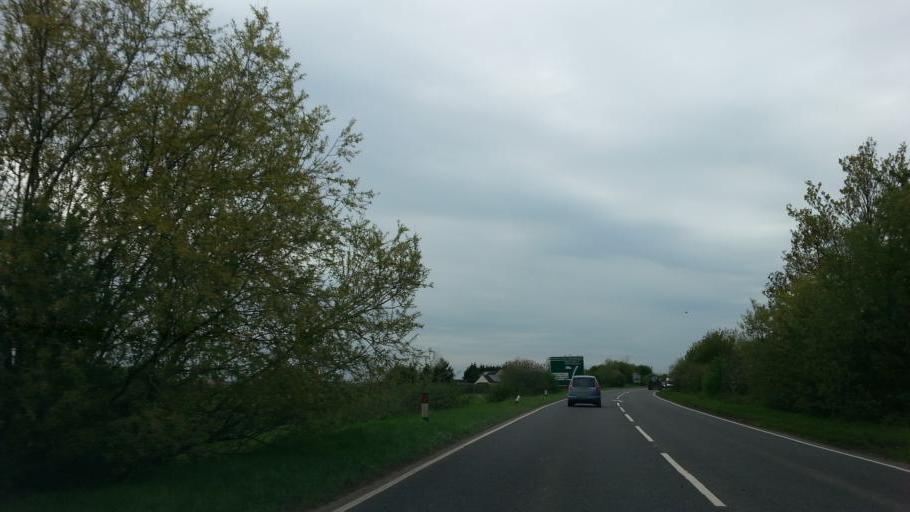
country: GB
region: England
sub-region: Cambridgeshire
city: March
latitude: 52.5306
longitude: 0.0722
